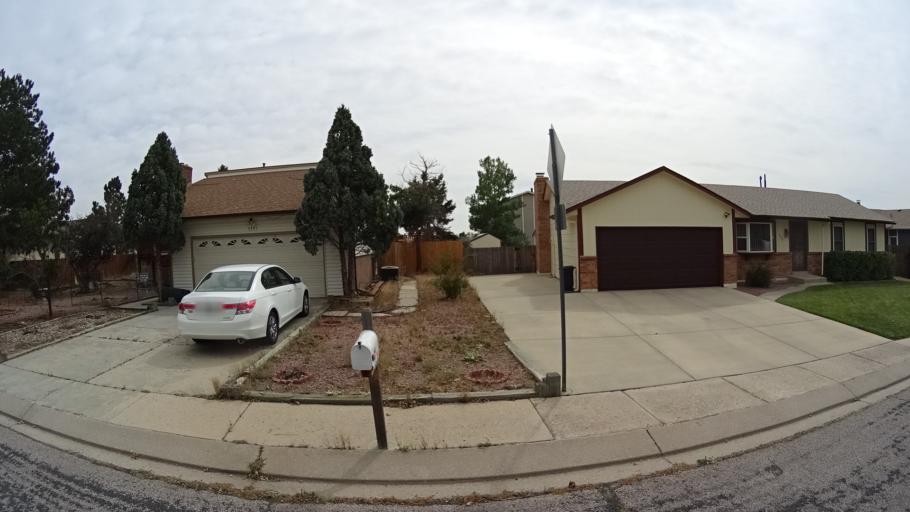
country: US
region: Colorado
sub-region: El Paso County
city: Cimarron Hills
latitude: 38.8969
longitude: -104.7285
